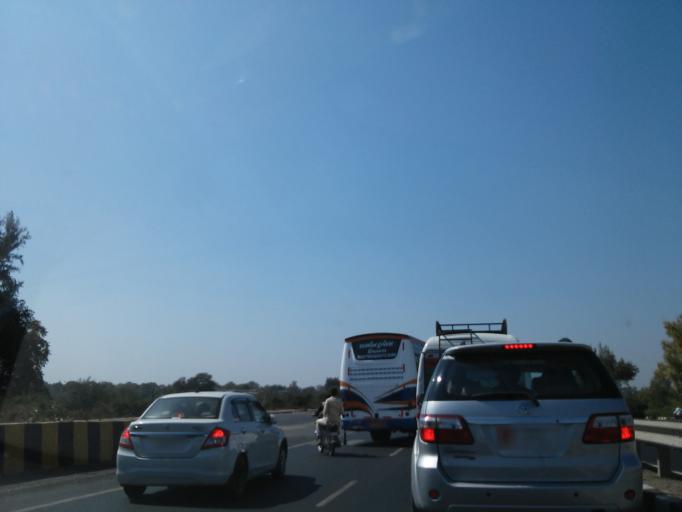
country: IN
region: Gujarat
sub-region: Gandhinagar
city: Chhala
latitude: 23.4437
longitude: 72.8499
